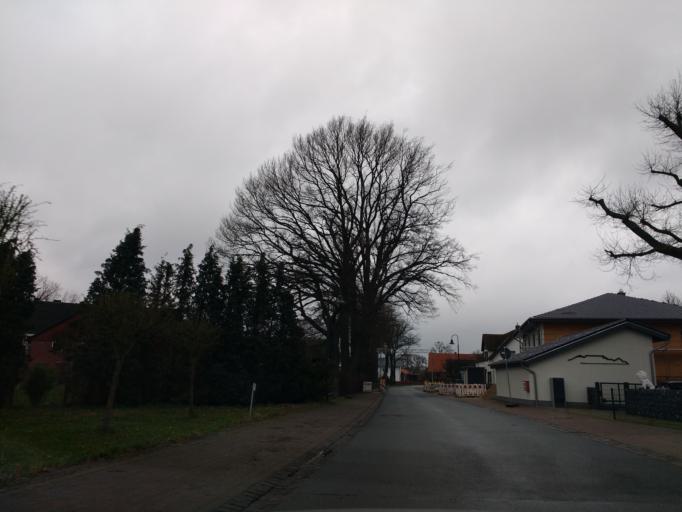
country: DE
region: North Rhine-Westphalia
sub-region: Regierungsbezirk Detmold
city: Salzkotten
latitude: 51.7058
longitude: 8.5811
